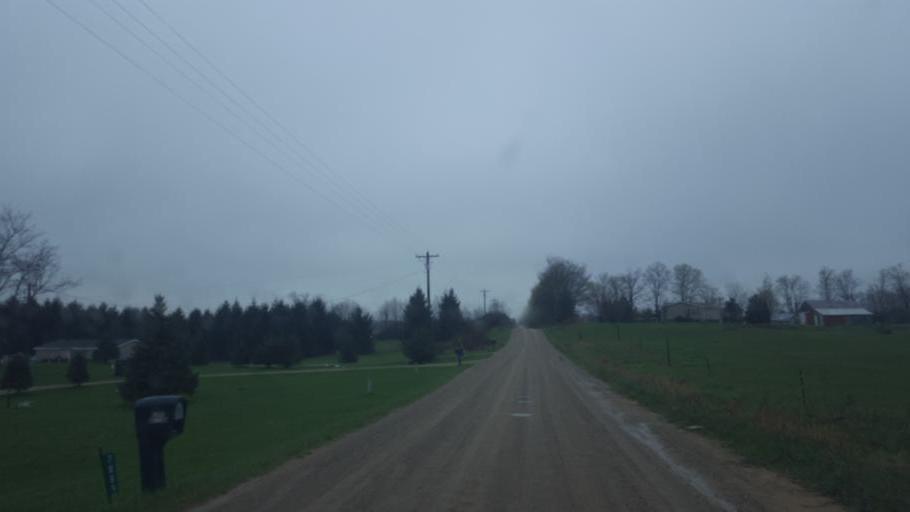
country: US
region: Michigan
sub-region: Isabella County
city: Lake Isabella
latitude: 43.5819
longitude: -85.0038
